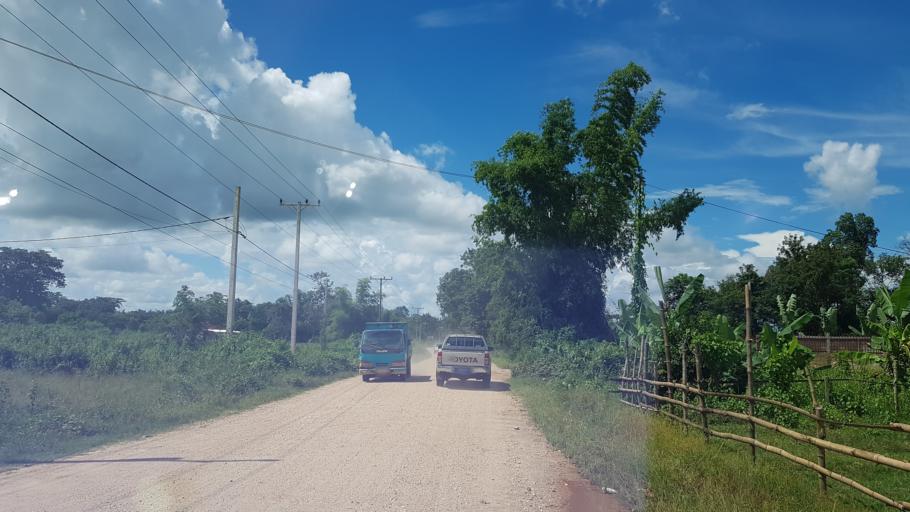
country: LA
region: Vientiane
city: Vientiane
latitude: 18.2200
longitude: 102.5170
